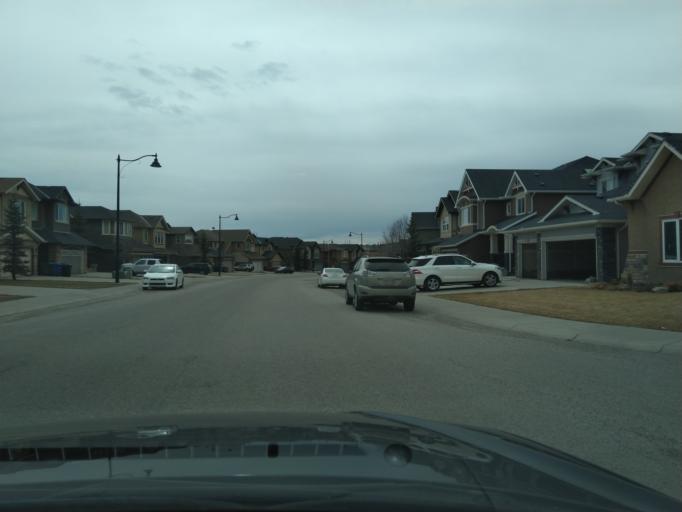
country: CA
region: Alberta
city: Calgary
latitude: 51.1674
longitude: -114.0808
